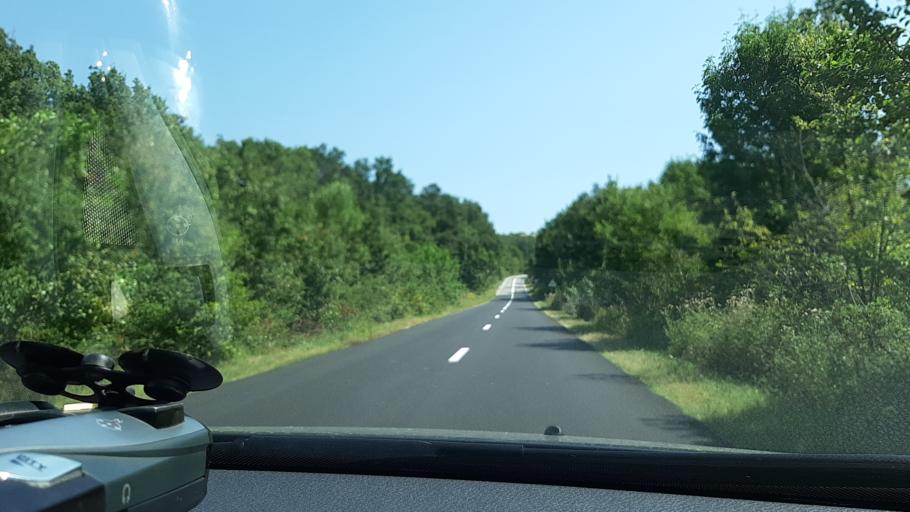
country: RO
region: Gorj
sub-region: Comuna Licuriciu
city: Licuriciu
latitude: 44.9447
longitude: 23.5849
